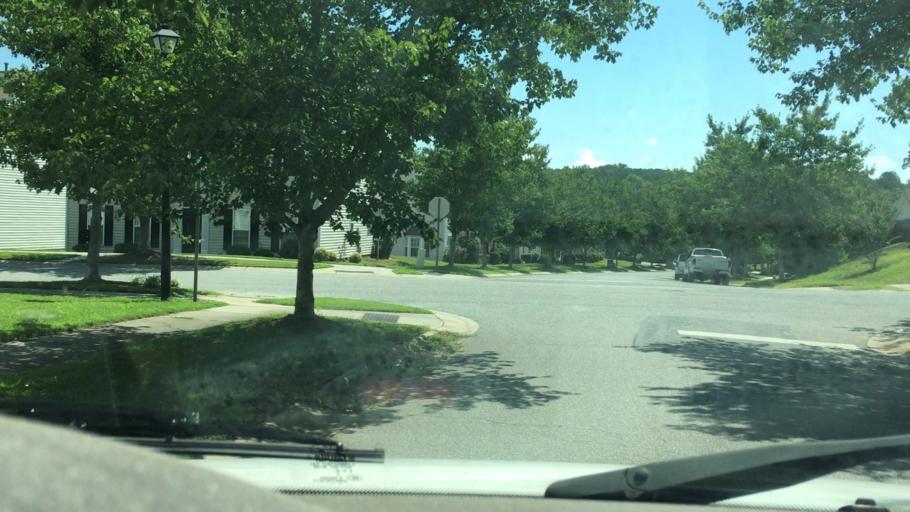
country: US
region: North Carolina
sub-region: Mecklenburg County
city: Huntersville
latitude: 35.3832
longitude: -80.9172
